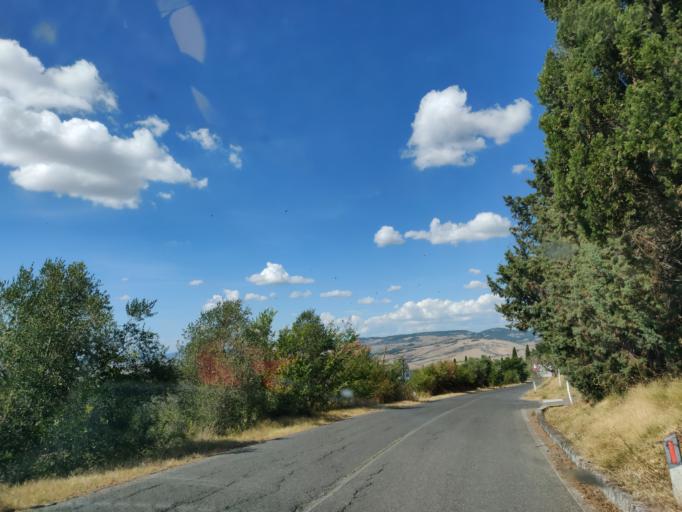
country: IT
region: Tuscany
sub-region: Provincia di Siena
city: Radicofani
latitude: 42.9711
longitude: 11.7362
